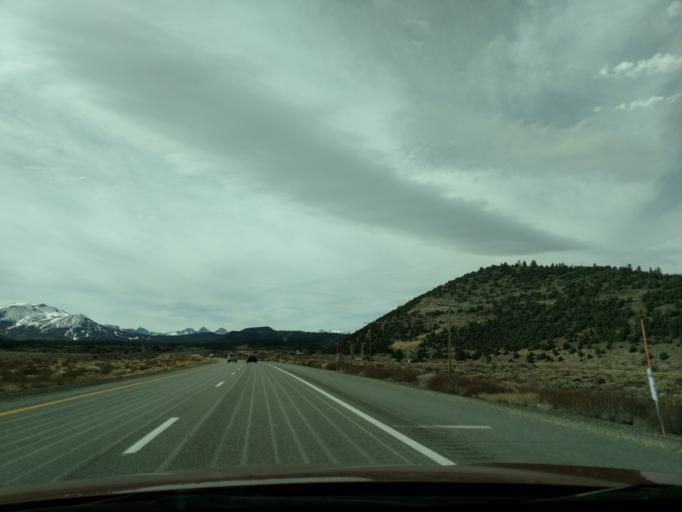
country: US
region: California
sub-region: Mono County
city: Mammoth Lakes
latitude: 37.6354
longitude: -118.8850
